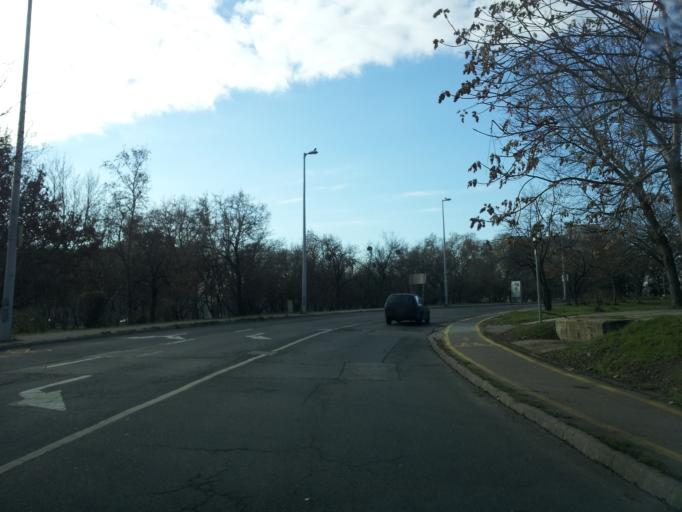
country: HU
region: Budapest
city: Budapest IX. keruelet
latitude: 47.4768
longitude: 19.0614
